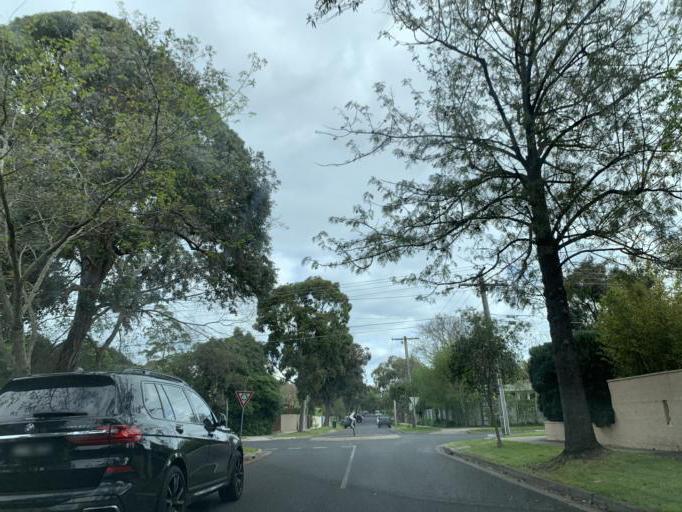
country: AU
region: Victoria
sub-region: Bayside
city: Cheltenham
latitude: -37.9714
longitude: 145.0410
